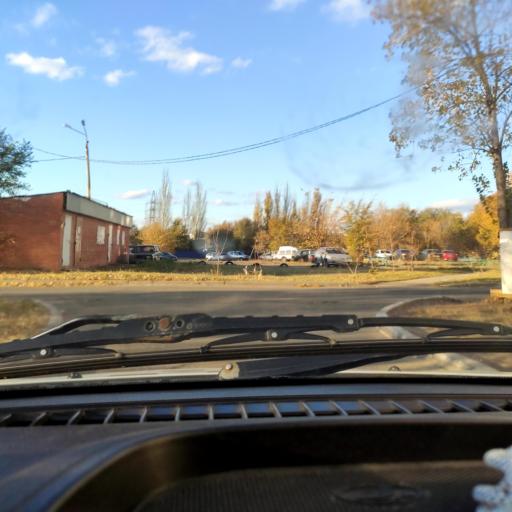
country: RU
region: Samara
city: Zhigulevsk
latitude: 53.4836
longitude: 49.5179
